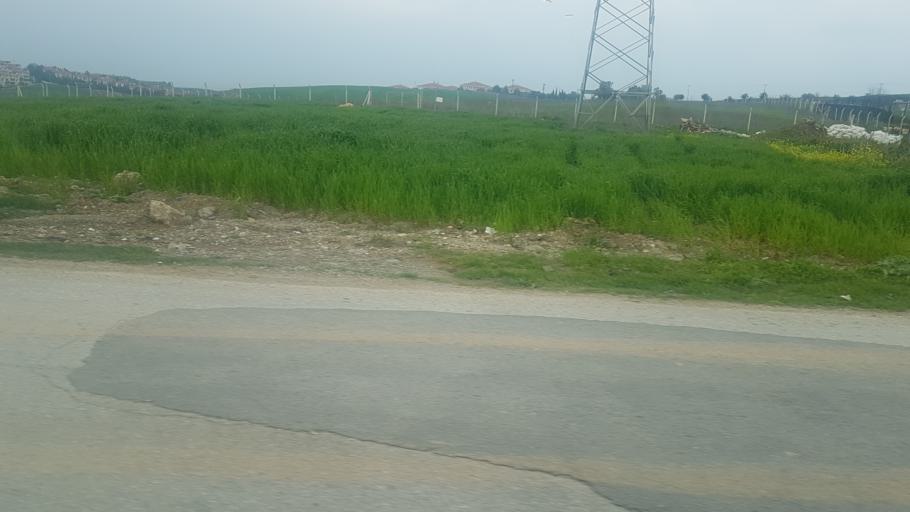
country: TR
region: Adana
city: Seyhan
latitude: 37.0580
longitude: 35.2415
